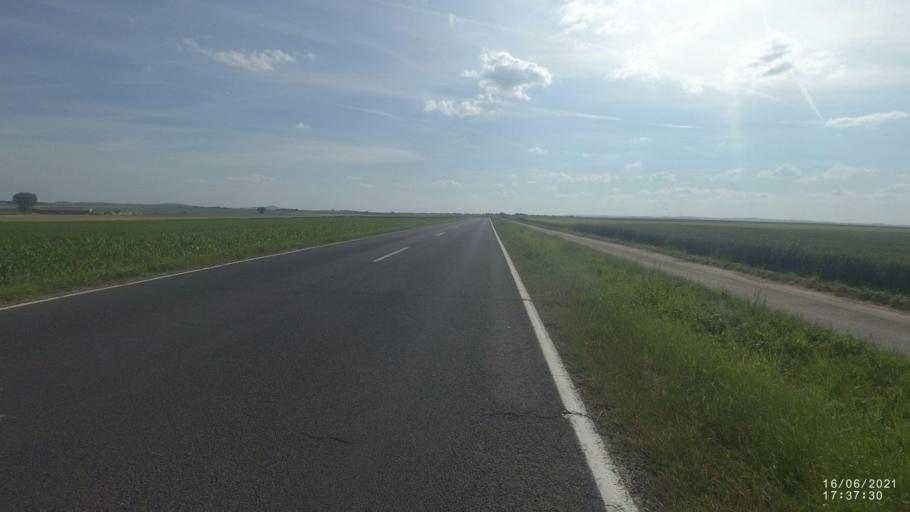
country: DE
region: Rheinland-Pfalz
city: Kalt
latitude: 50.2692
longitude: 7.4146
